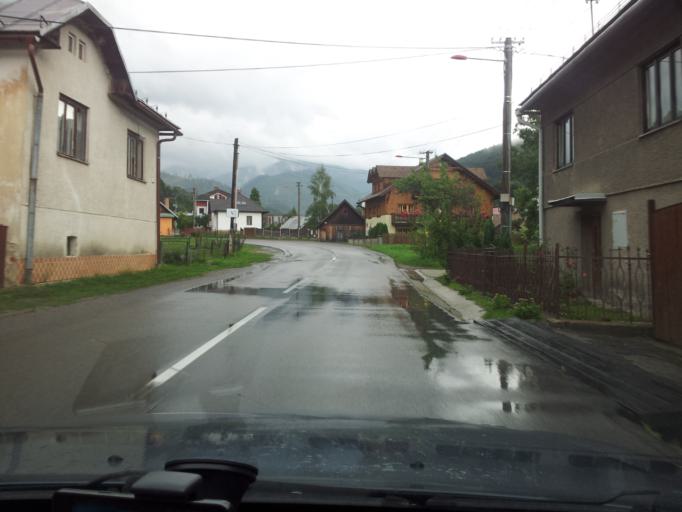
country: SK
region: Banskobystricky
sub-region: Okres Banska Bystrica
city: Brezno
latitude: 48.8526
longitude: 19.6326
